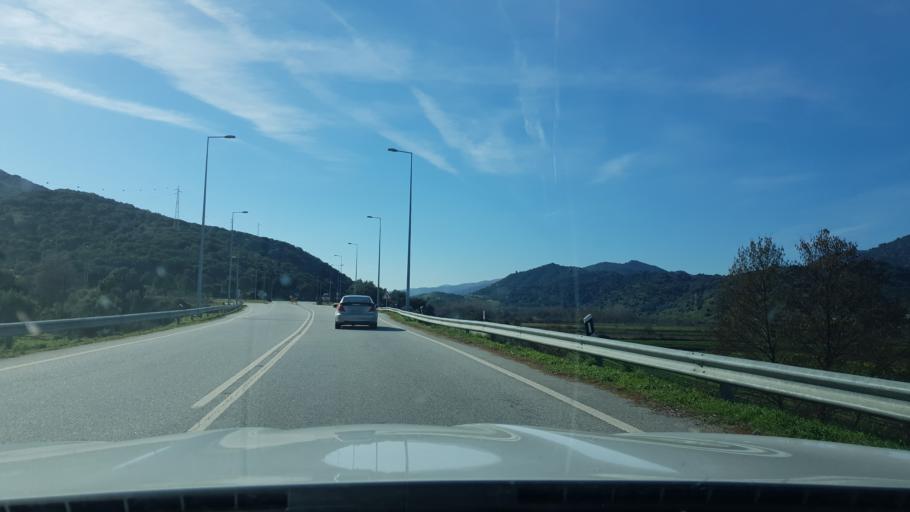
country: PT
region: Braganca
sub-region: Torre de Moncorvo
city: Torre de Moncorvo
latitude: 41.1829
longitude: -7.1025
